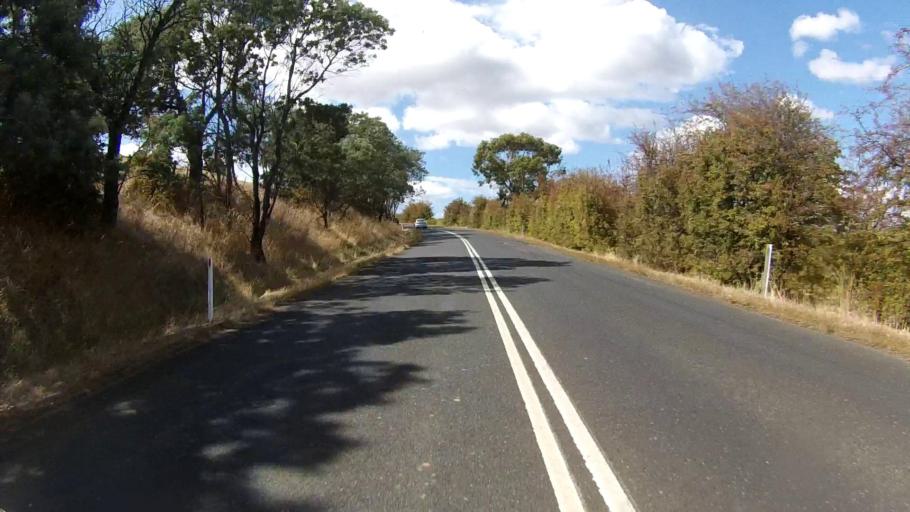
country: AU
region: Tasmania
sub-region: Derwent Valley
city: New Norfolk
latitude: -42.7373
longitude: 146.9312
